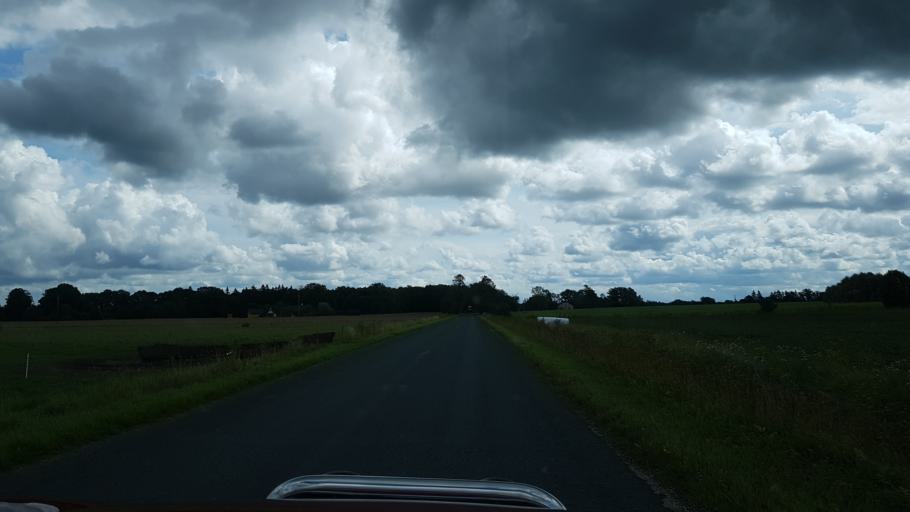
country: EE
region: Laeaene
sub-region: Lihula vald
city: Lihula
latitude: 58.7095
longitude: 24.0159
